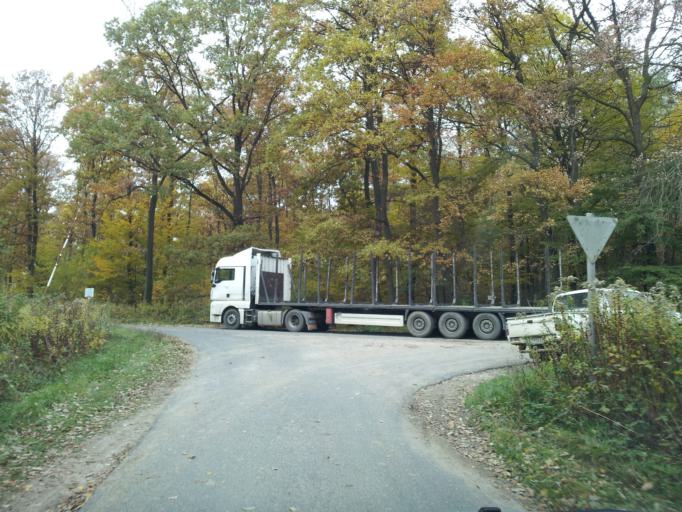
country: HU
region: Gyor-Moson-Sopron
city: Pannonhalma
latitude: 47.4949
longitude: 17.7146
